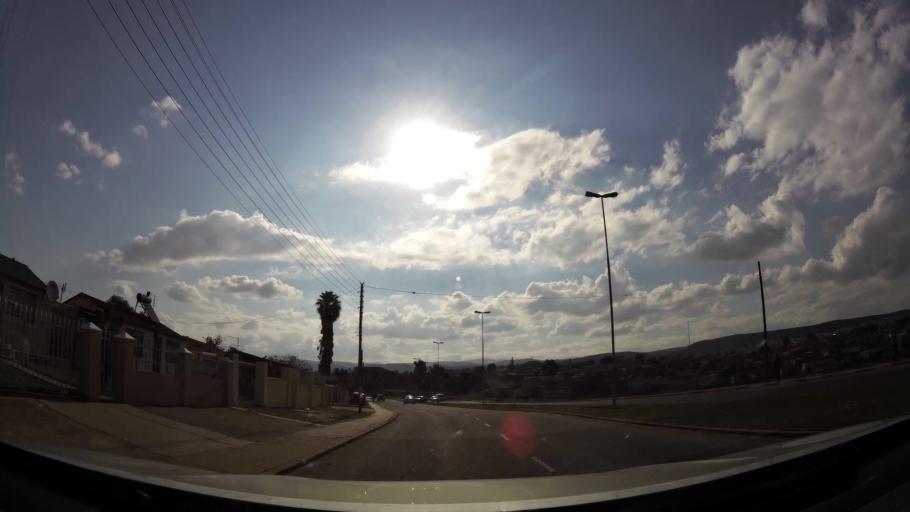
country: ZA
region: Eastern Cape
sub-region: Nelson Mandela Bay Metropolitan Municipality
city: Uitenhage
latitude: -33.7453
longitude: 25.3806
